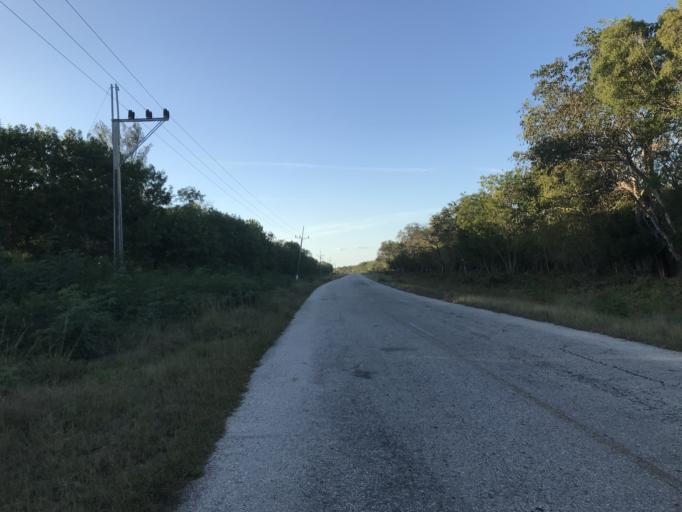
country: CU
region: Cienfuegos
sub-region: Municipio de Aguada de Pasajeros
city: Aguada de Pasajeros
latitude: 22.0701
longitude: -81.0533
